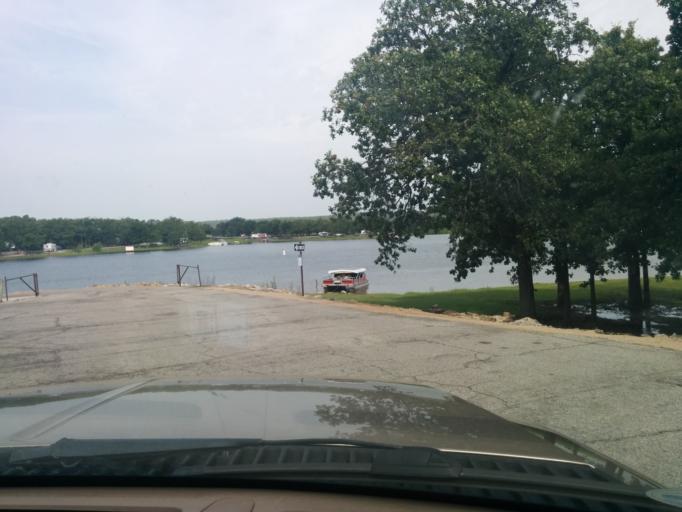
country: US
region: Oklahoma
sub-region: Osage County
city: Skiatook
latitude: 36.3223
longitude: -96.1114
